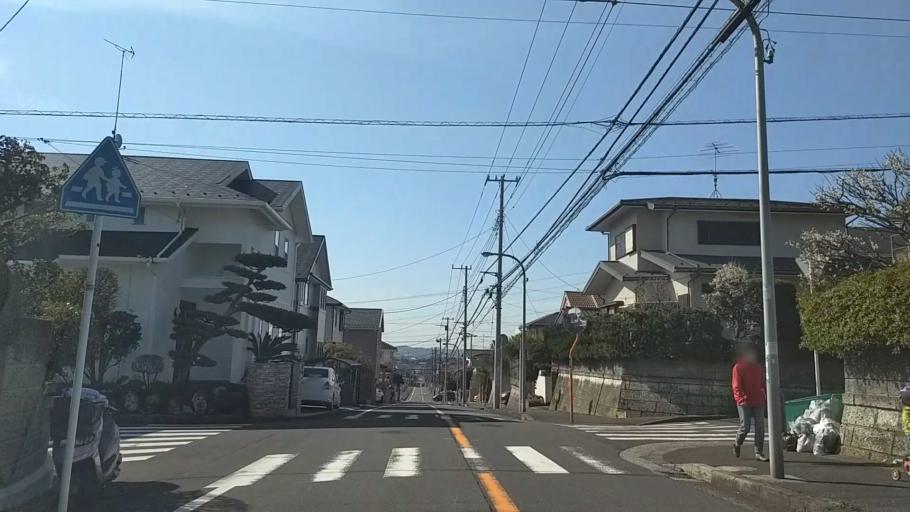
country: JP
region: Kanagawa
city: Kamakura
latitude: 35.3806
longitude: 139.5508
